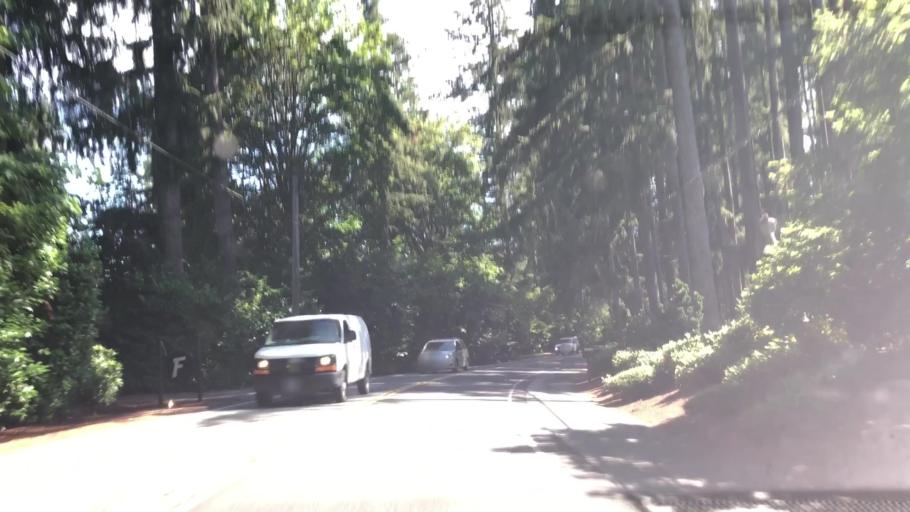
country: US
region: Washington
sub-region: King County
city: Cottage Lake
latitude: 47.7288
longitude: -122.0749
